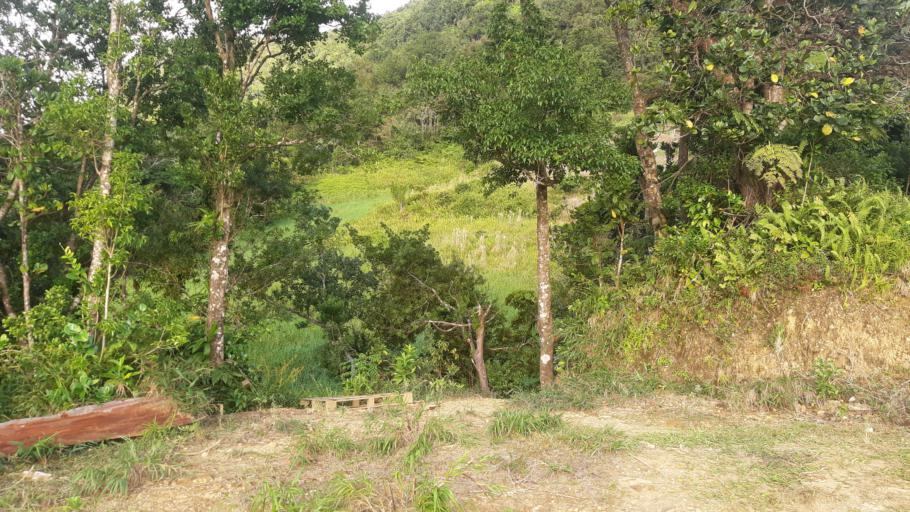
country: GP
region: Guadeloupe
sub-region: Guadeloupe
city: Saint-Claude
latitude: 16.0468
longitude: -61.6828
